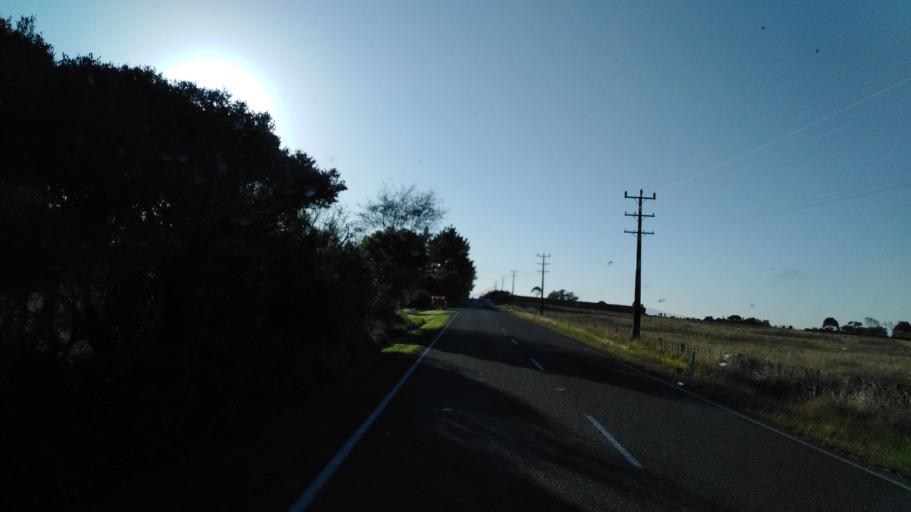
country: NZ
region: Manawatu-Wanganui
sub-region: Rangitikei District
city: Bulls
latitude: -40.0675
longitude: 175.4046
